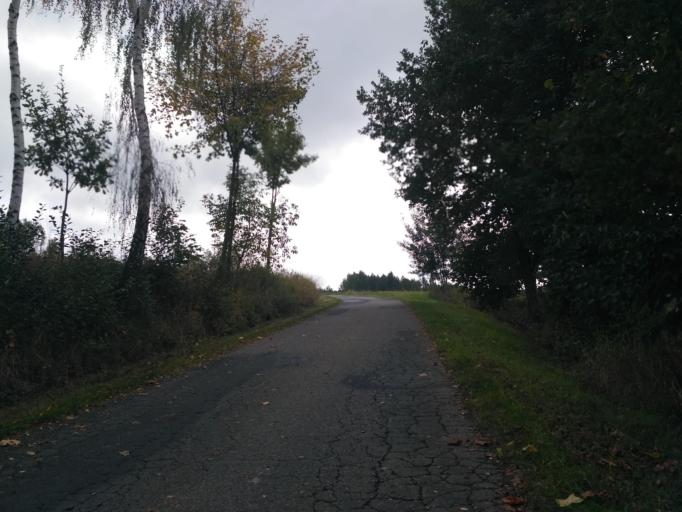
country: PL
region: Subcarpathian Voivodeship
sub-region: Powiat ropczycko-sedziszowski
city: Niedzwiada
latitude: 49.9299
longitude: 21.4793
